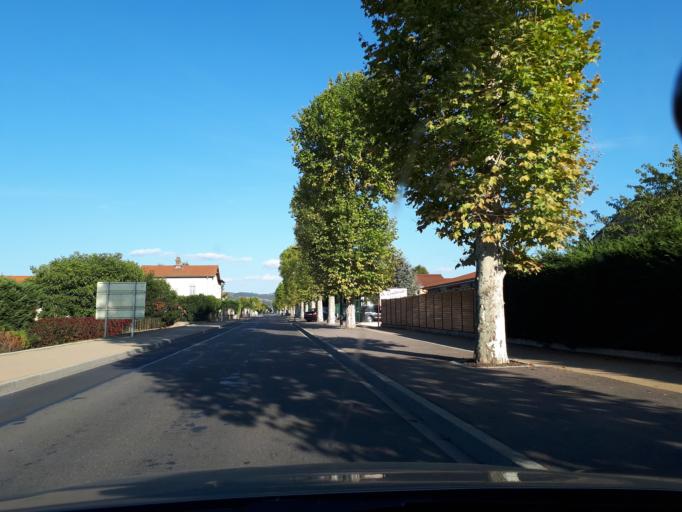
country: FR
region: Rhone-Alpes
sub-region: Departement de la Loire
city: Saint-Andre-le-Puy
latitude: 45.6451
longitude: 4.2549
